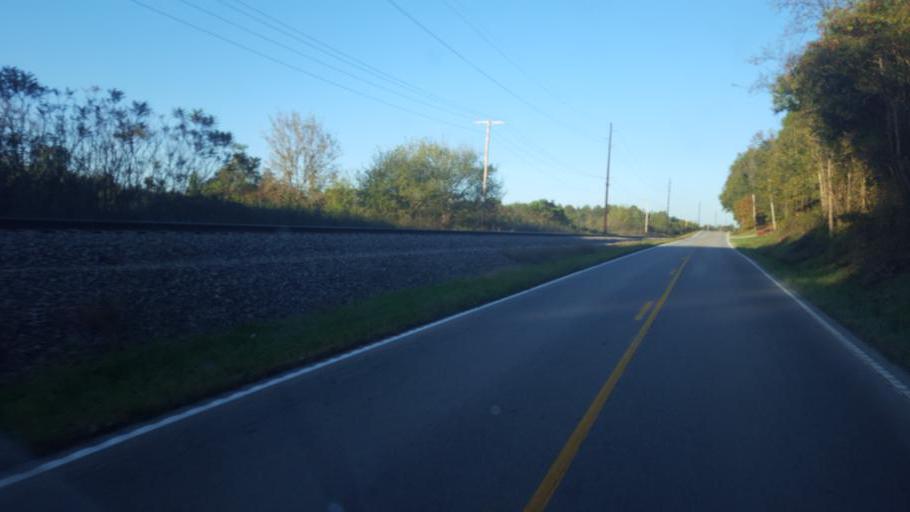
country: US
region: Ohio
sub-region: Scioto County
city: West Portsmouth
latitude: 38.6723
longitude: -83.0855
